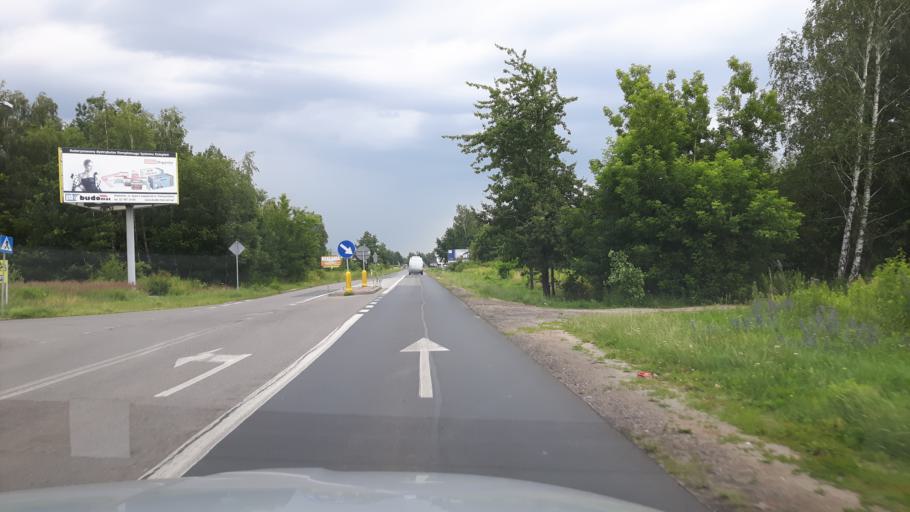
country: PL
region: Masovian Voivodeship
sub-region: Powiat wolominski
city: Wolomin
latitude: 52.3425
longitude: 21.2600
